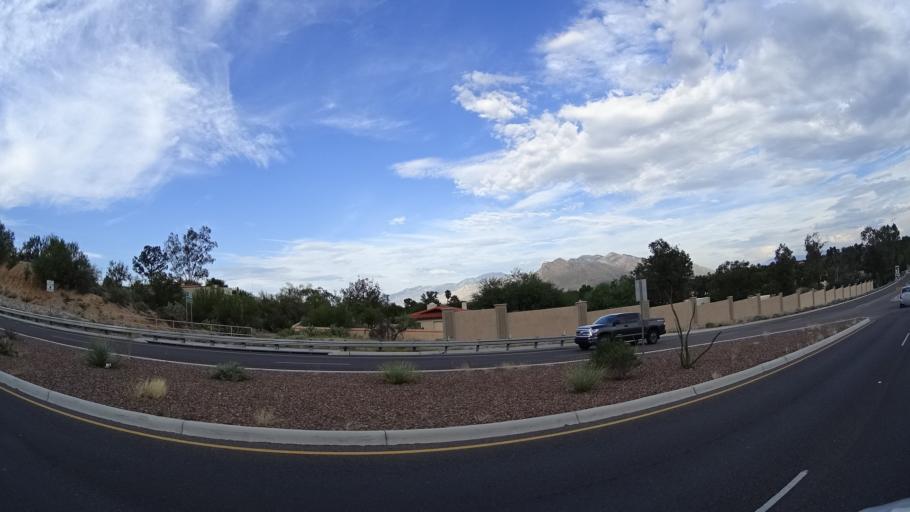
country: US
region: Arizona
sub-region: Pima County
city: Casas Adobes
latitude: 32.3532
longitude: -111.0316
